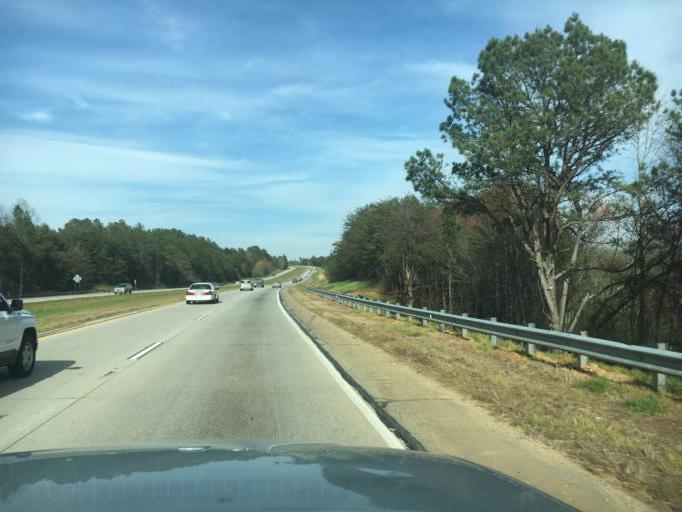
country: US
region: Georgia
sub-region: Hall County
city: Lula
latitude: 34.3752
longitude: -83.7226
